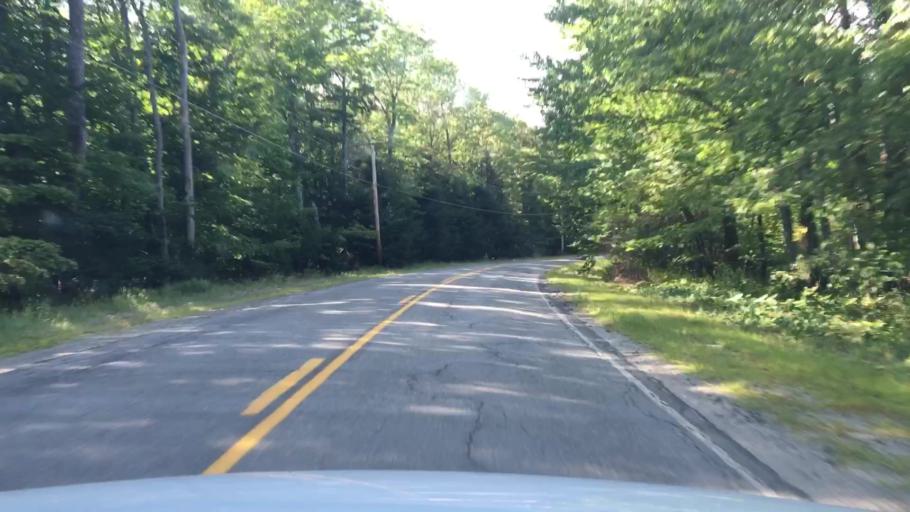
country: US
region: Maine
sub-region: Penobscot County
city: Enfield
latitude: 45.2179
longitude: -68.5342
